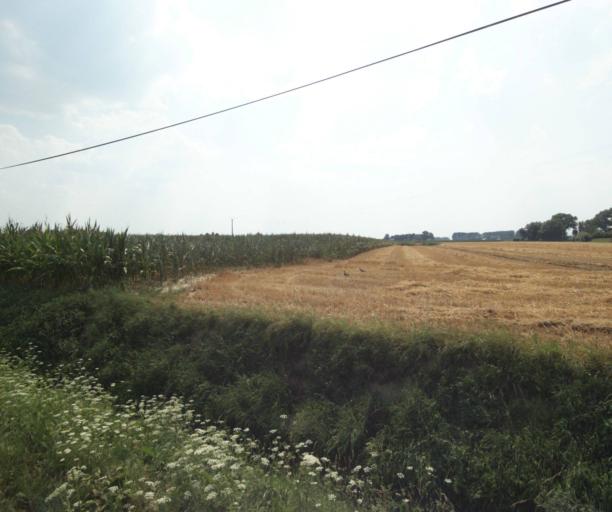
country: FR
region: Nord-Pas-de-Calais
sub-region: Departement du Nord
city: Quesnoy-sur-Deule
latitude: 50.7312
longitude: 2.9962
